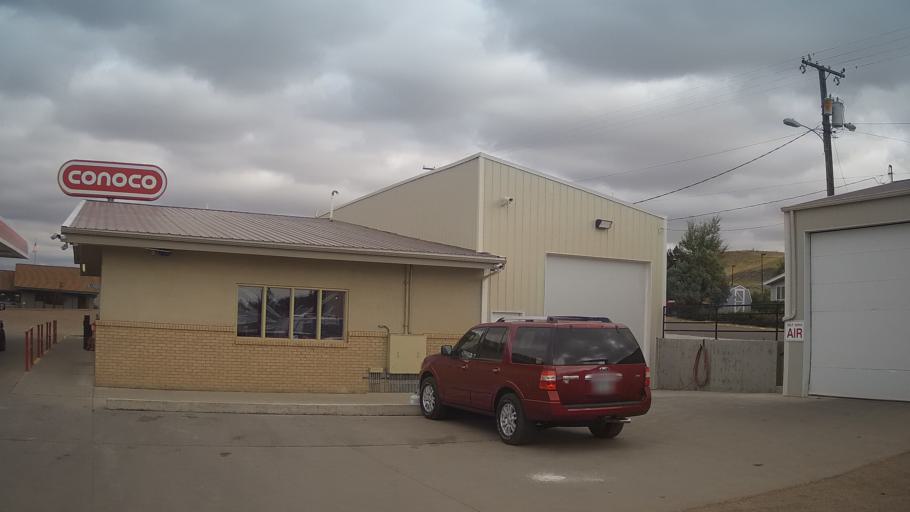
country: US
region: Montana
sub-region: Valley County
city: Glasgow
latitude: 48.2094
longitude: -106.6412
